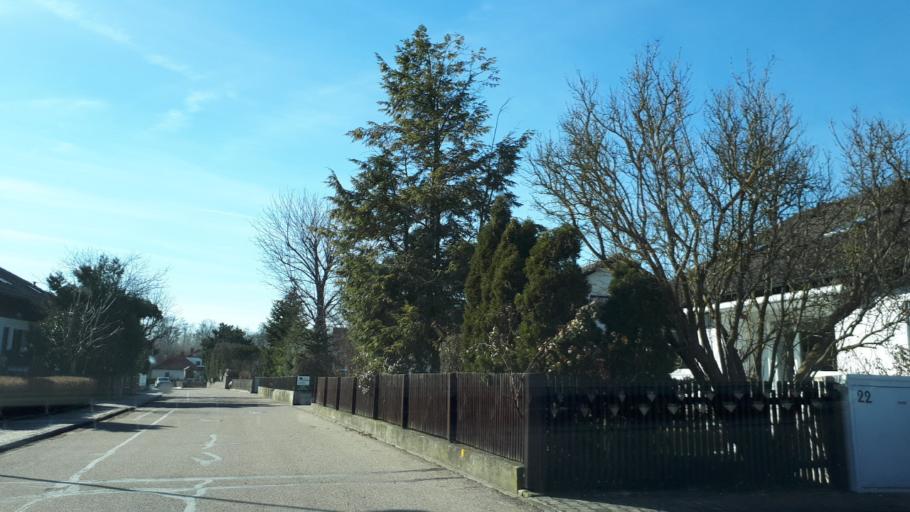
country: DE
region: Bavaria
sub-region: Upper Palatinate
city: Pentling
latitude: 48.9872
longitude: 12.0548
